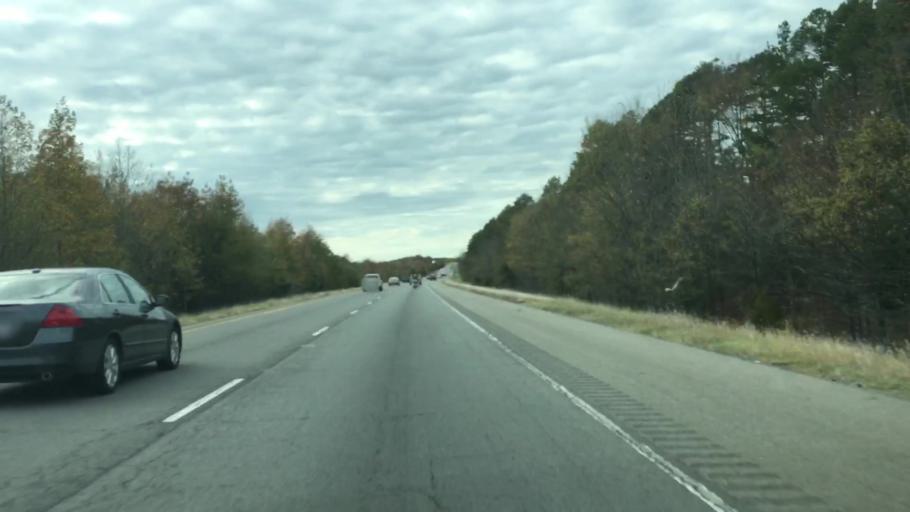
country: US
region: Arkansas
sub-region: Faulkner County
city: Conway
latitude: 35.1209
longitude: -92.4861
